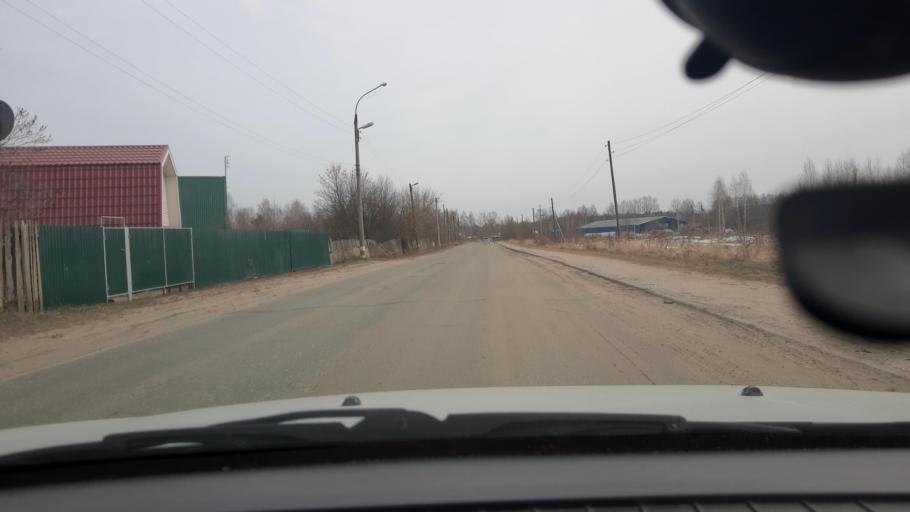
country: RU
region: Nizjnij Novgorod
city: Gidrotorf
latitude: 56.4657
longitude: 43.5437
